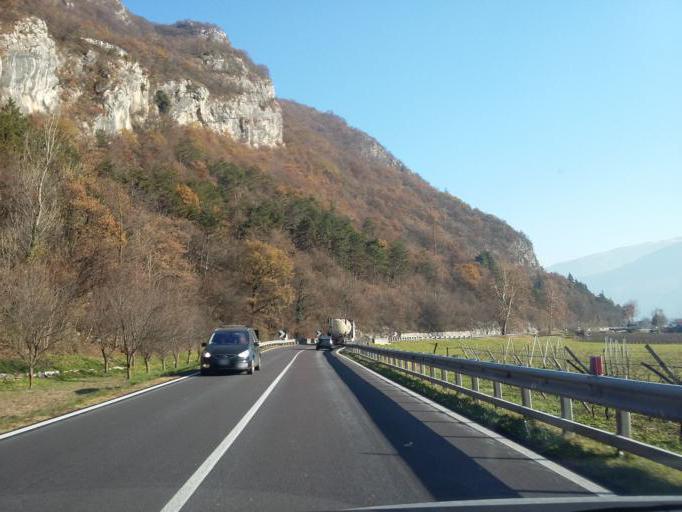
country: IT
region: Trentino-Alto Adige
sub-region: Provincia di Trento
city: Ronzo-Chienis
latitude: 45.8552
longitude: 10.9407
